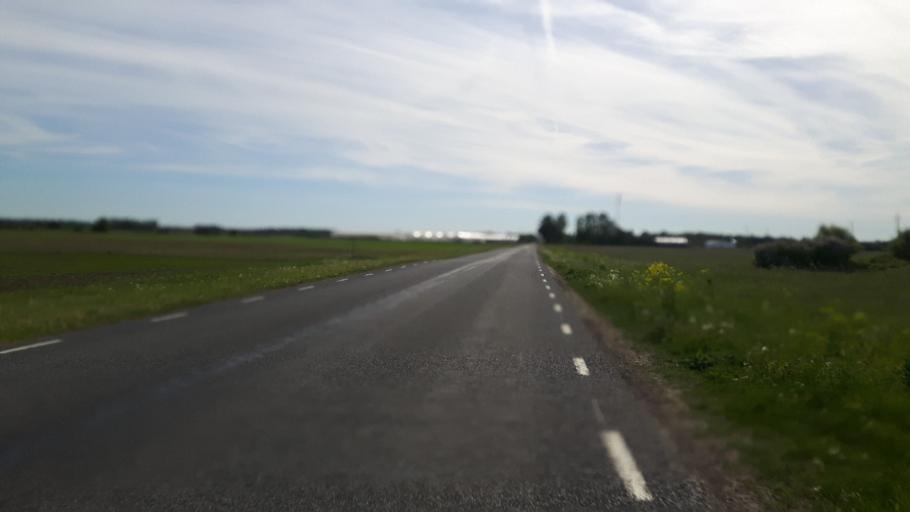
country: EE
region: Harju
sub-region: Raasiku vald
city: Arukula
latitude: 59.4326
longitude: 25.1173
